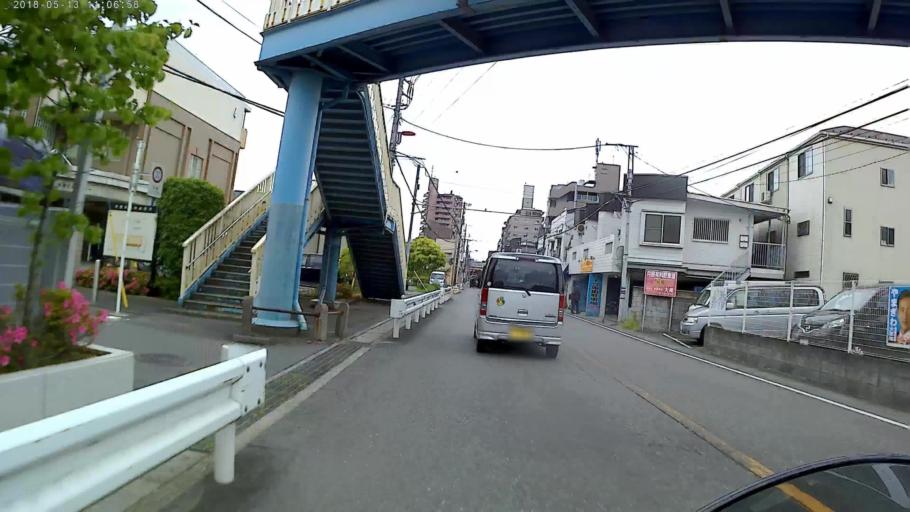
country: JP
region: Tokyo
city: Chofugaoka
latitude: 35.5884
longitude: 139.6177
